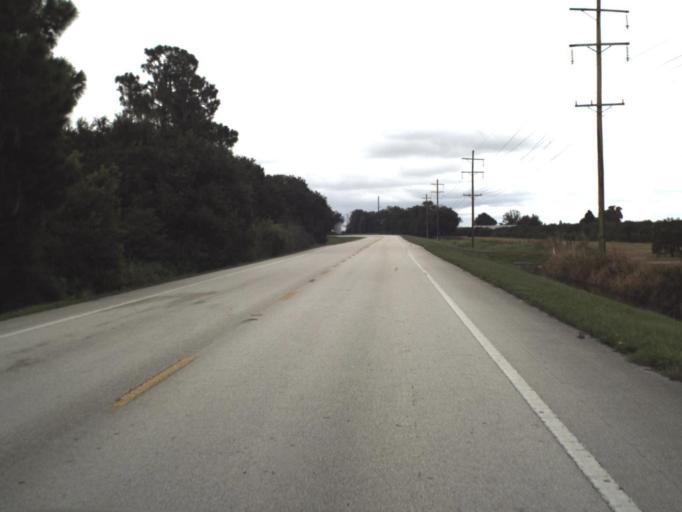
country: US
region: Florida
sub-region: Hillsborough County
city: Wimauma
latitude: 27.5885
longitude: -82.1004
